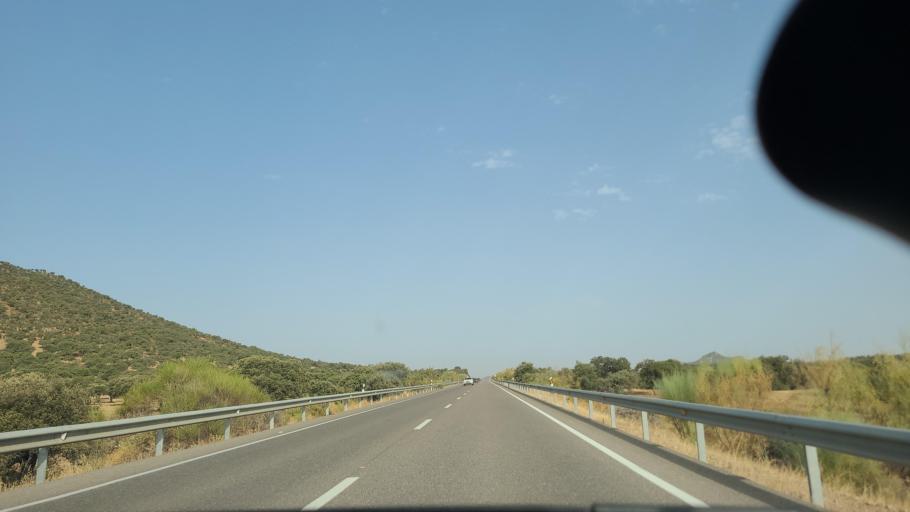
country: ES
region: Andalusia
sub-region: Province of Cordoba
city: Belmez
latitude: 38.2228
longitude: -5.1556
